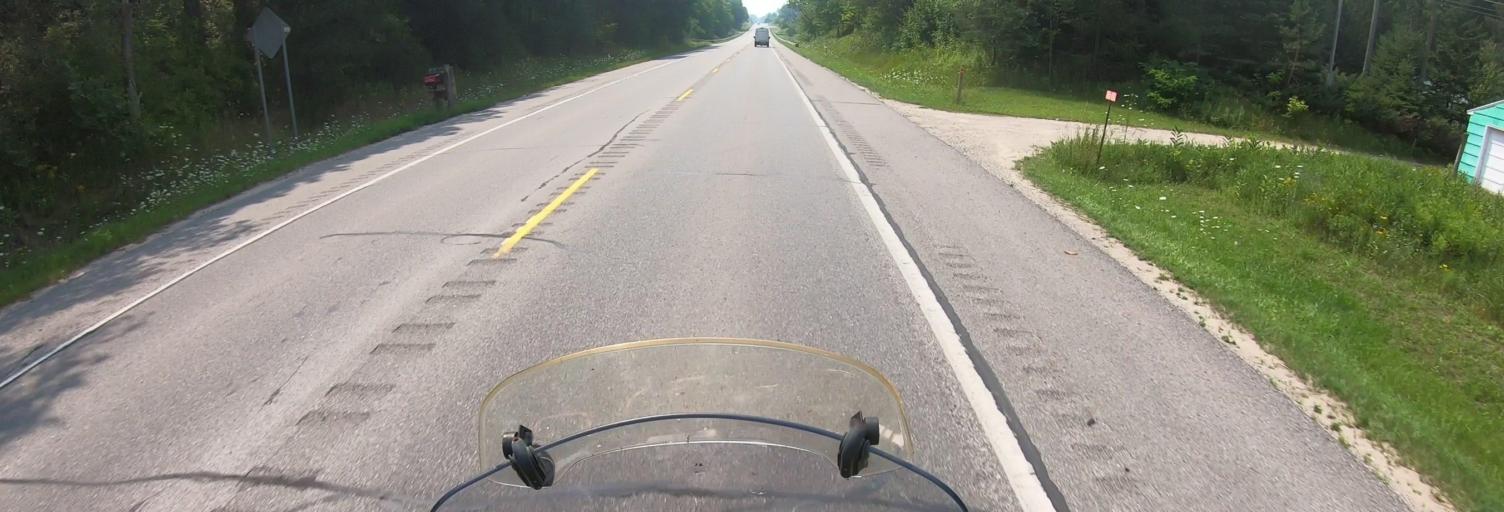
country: US
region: Michigan
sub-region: Luce County
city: Newberry
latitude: 46.3231
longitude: -85.5097
